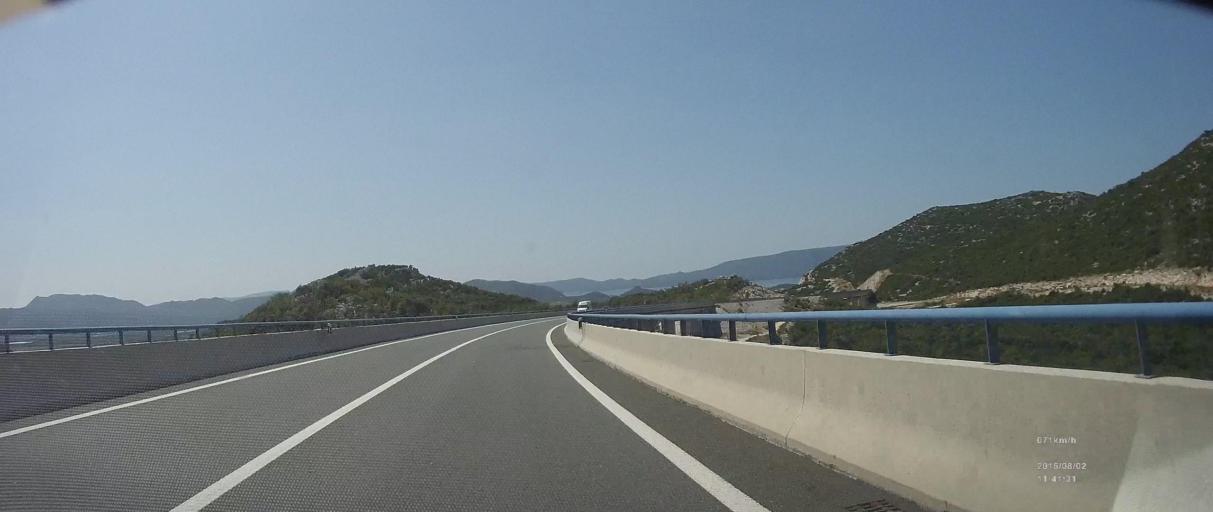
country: HR
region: Dubrovacko-Neretvanska
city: Komin
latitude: 43.0628
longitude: 17.4958
